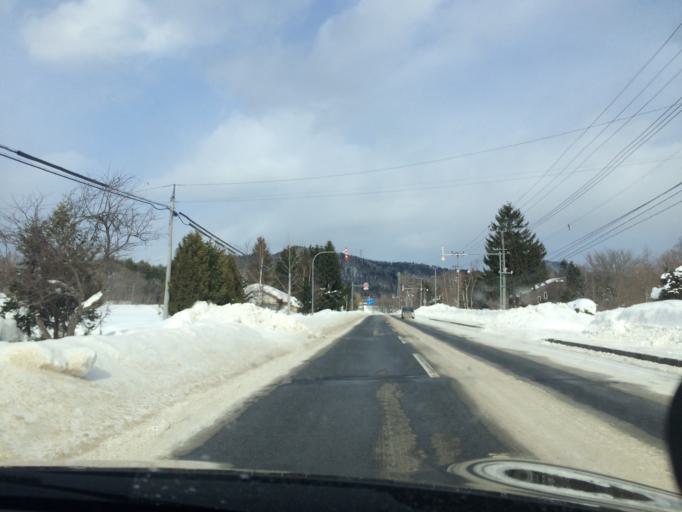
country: JP
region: Hokkaido
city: Shimo-furano
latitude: 42.9996
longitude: 142.4053
